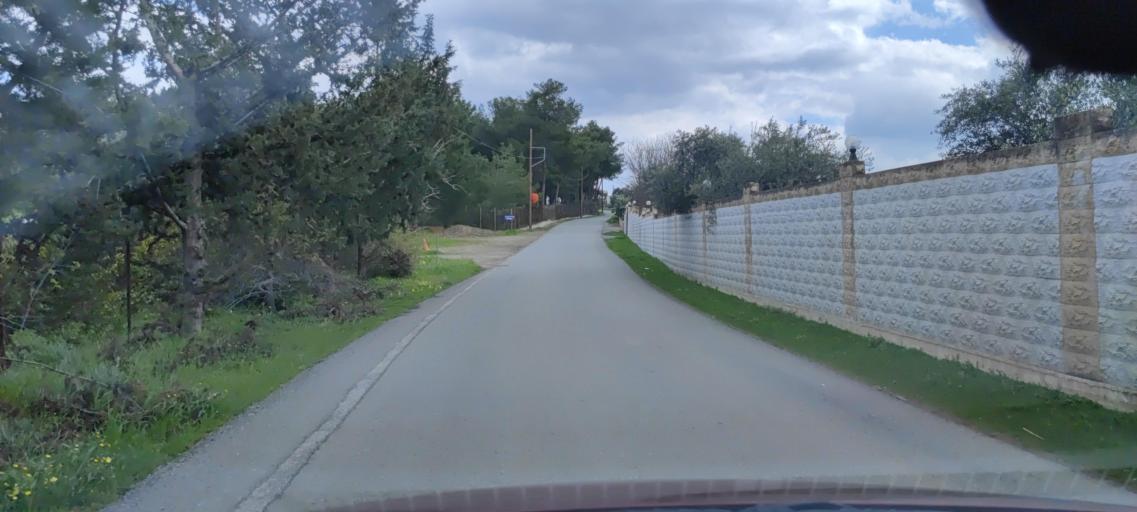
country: CY
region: Lefkosia
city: Lythrodontas
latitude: 34.9401
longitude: 33.3145
